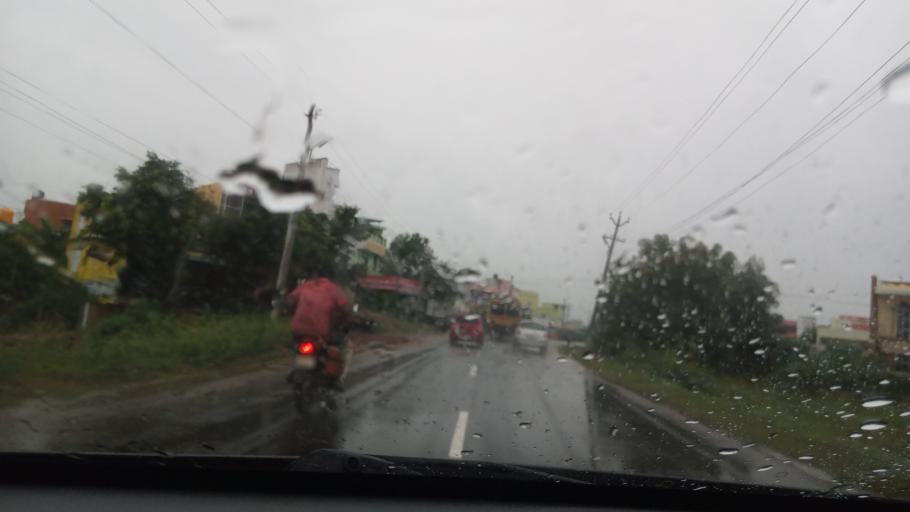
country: IN
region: Tamil Nadu
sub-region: Tiruvannamalai
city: Cheyyar
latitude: 12.6687
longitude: 79.5363
